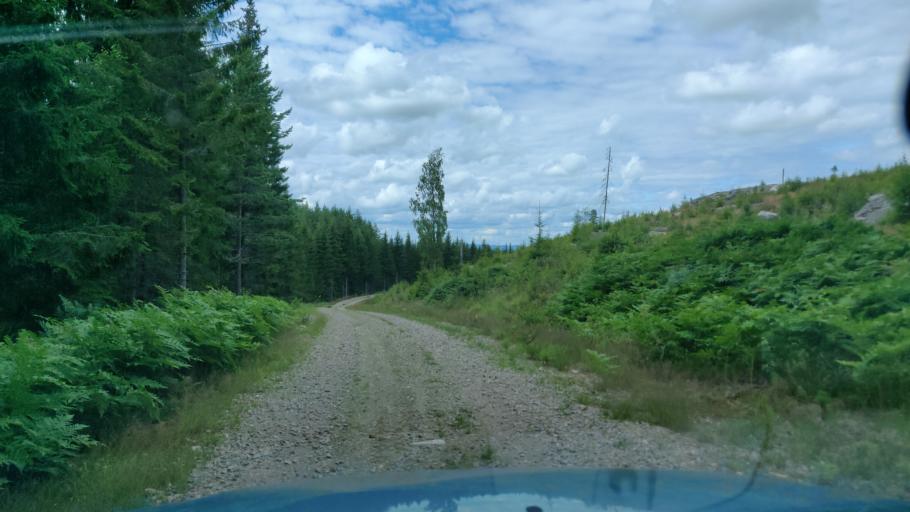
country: SE
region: Vaermland
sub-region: Hagfors Kommun
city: Hagfors
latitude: 59.9671
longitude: 13.5837
